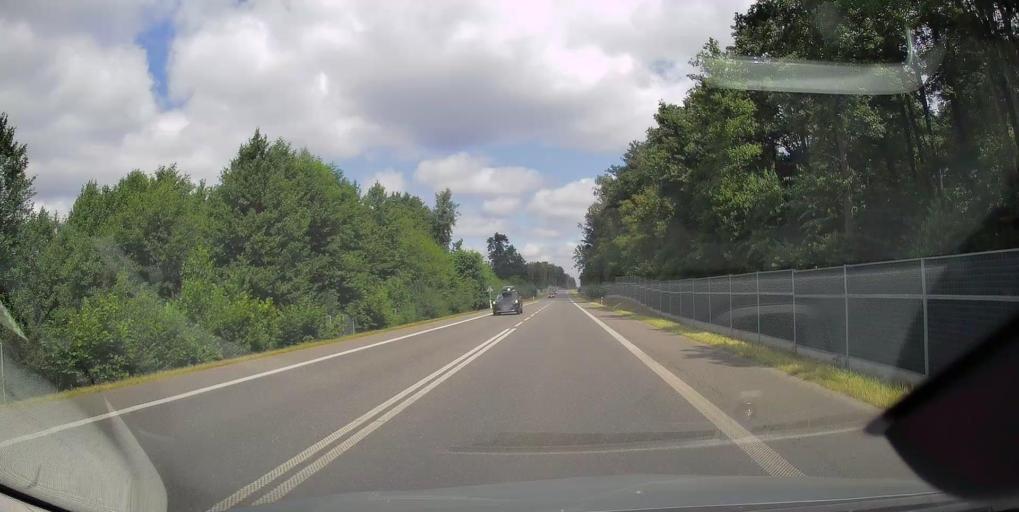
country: PL
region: Subcarpathian Voivodeship
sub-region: Powiat mielecki
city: Przeclaw
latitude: 50.2596
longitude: 21.4923
